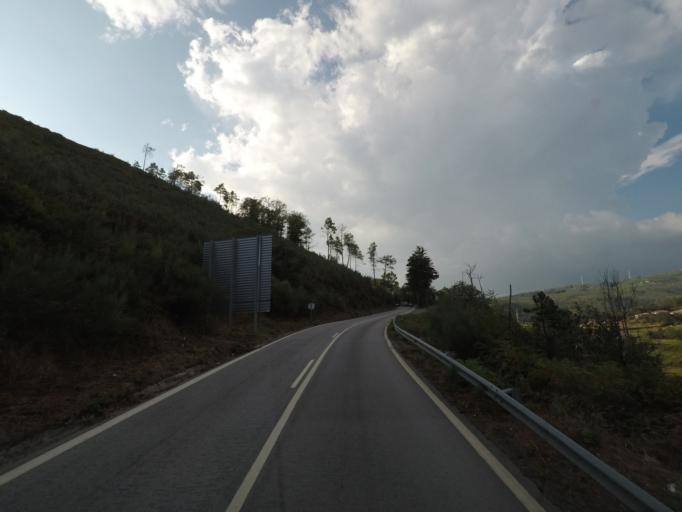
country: PT
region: Porto
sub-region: Baiao
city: Valadares
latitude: 41.1848
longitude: -7.9387
